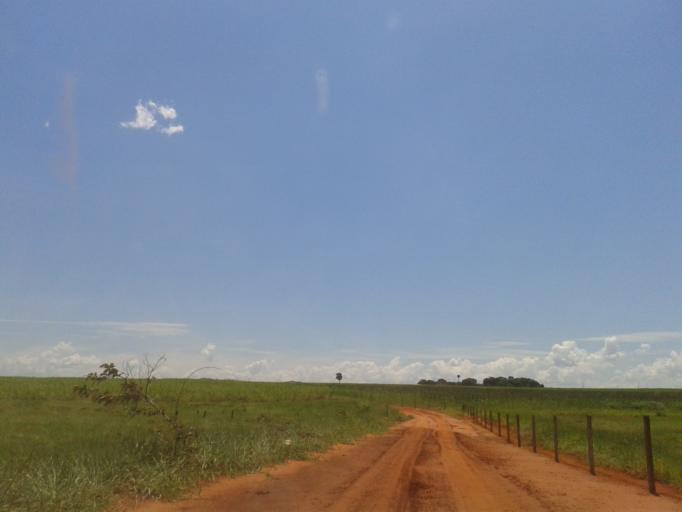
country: BR
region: Minas Gerais
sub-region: Santa Vitoria
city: Santa Vitoria
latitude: -19.1609
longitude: -50.4129
